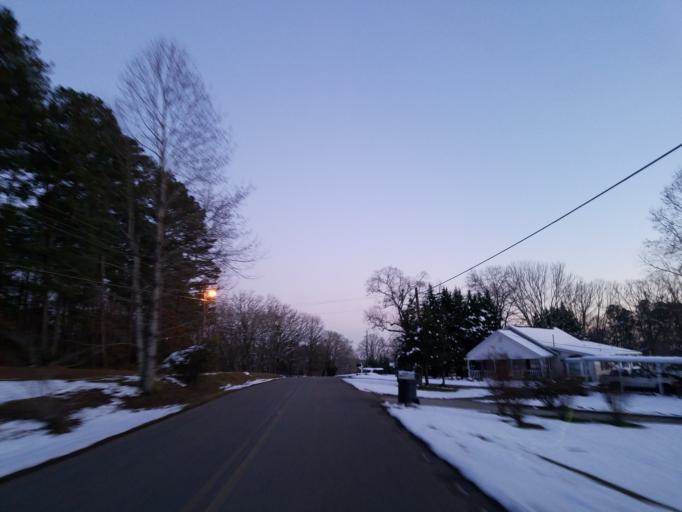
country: US
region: Georgia
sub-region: Pickens County
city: Nelson
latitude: 34.3628
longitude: -84.3710
